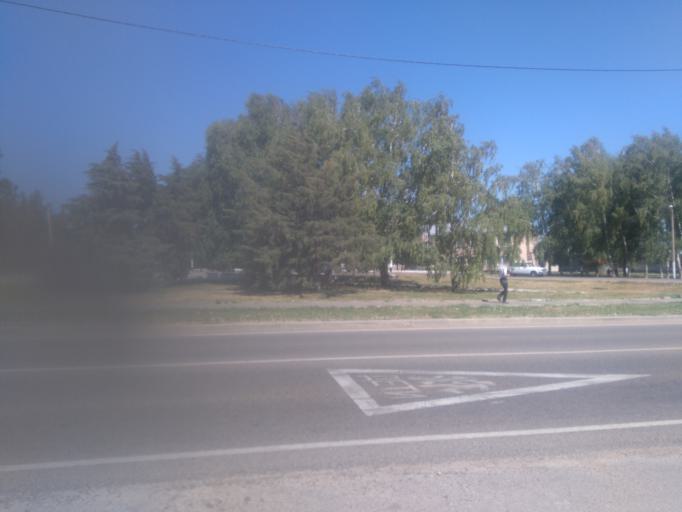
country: RU
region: Krasnodarskiy
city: Fastovetskaya
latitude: 45.9166
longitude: 40.1545
